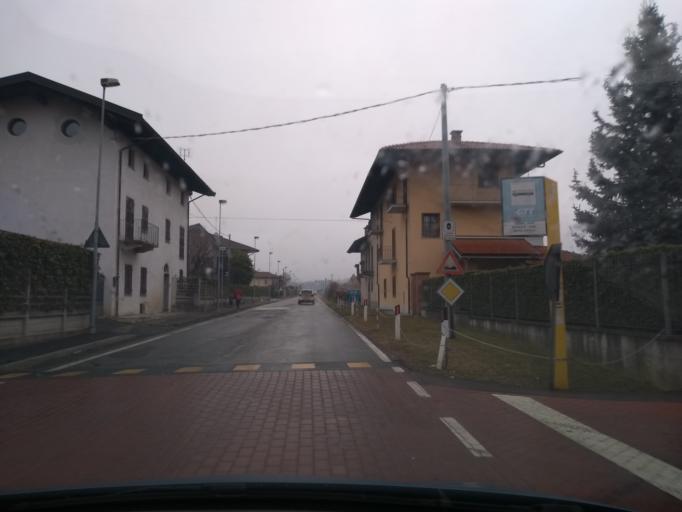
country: IT
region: Piedmont
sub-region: Provincia di Torino
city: Valperga
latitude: 45.3745
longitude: 7.6580
